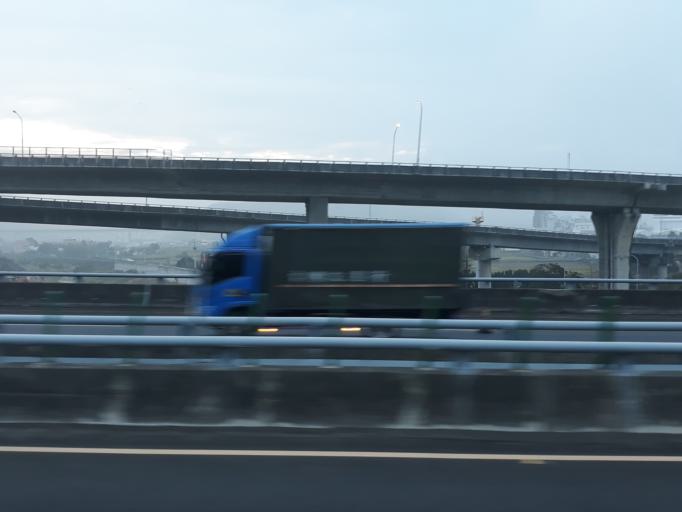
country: TW
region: Taiwan
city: Fengyuan
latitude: 24.3574
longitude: 120.7355
